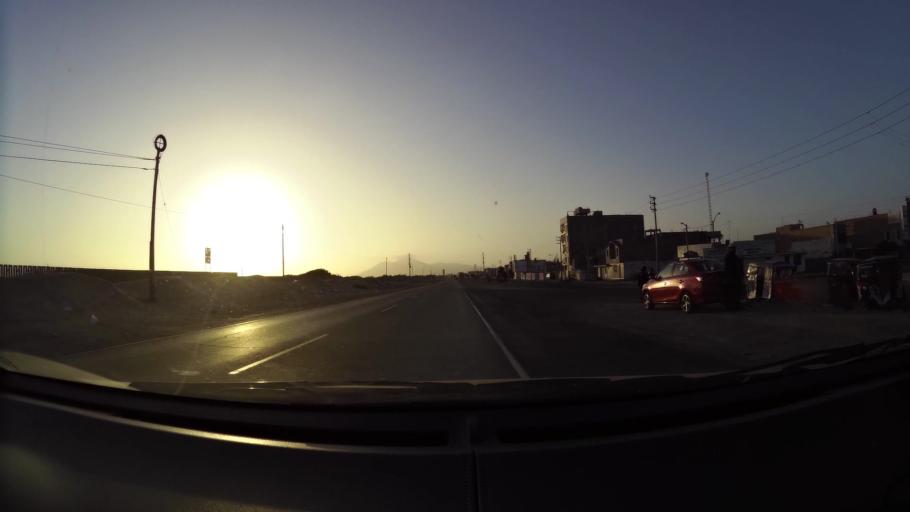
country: PE
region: Ancash
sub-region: Provincia de Santa
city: Buenos Aires
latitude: -9.1363
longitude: -78.5226
